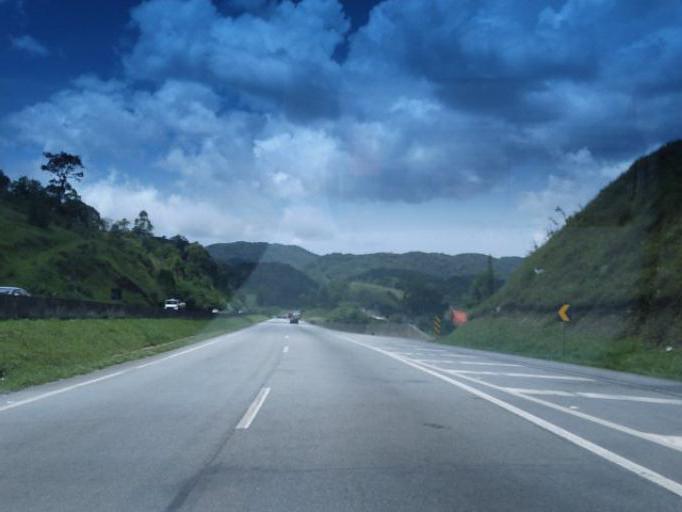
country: BR
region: Sao Paulo
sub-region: Juquitiba
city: Juquitiba
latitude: -24.0120
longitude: -47.1663
